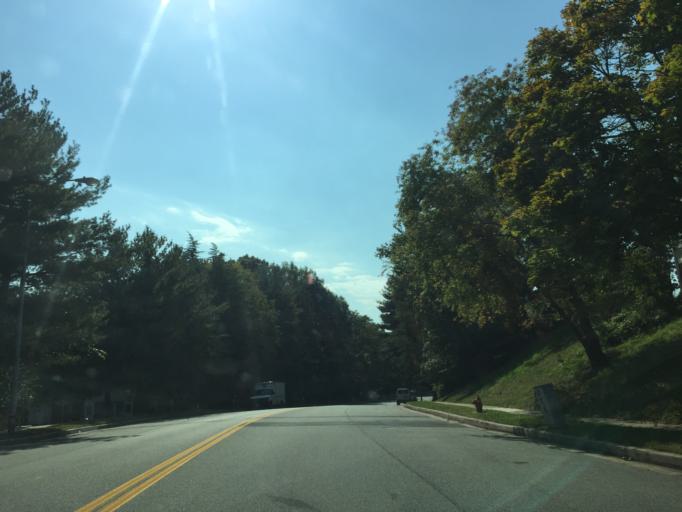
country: US
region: Maryland
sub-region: Baltimore County
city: Carney
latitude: 39.3837
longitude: -76.5045
